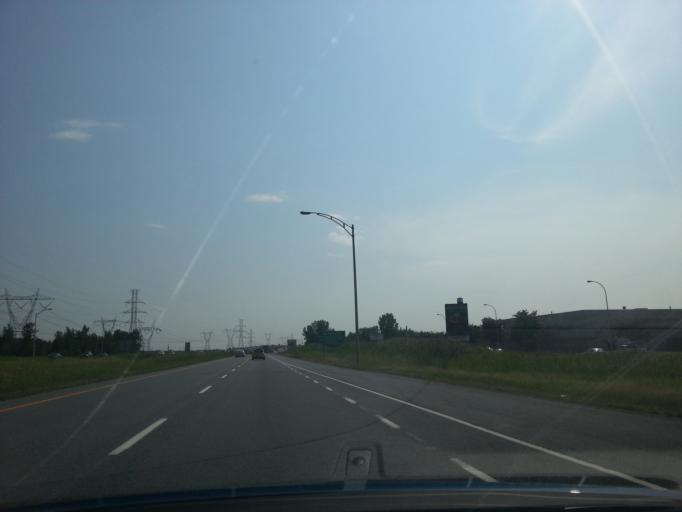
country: CA
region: Quebec
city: Saint-Bruno-de-Montarville
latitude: 45.4751
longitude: -73.3885
